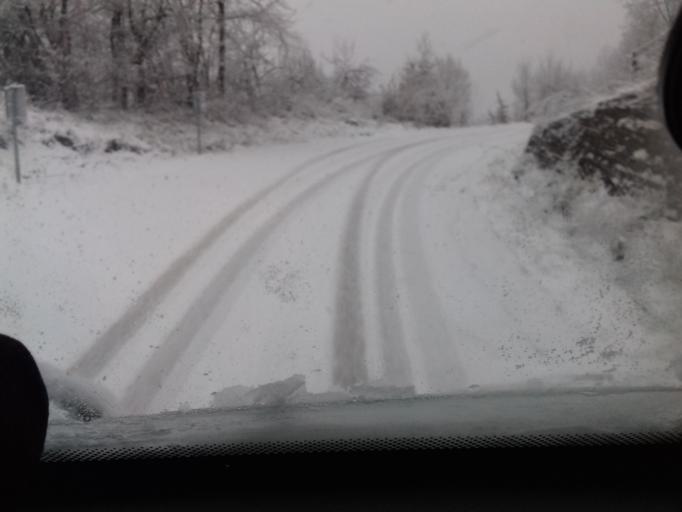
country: BA
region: Federation of Bosnia and Herzegovina
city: Lokvine
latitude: 44.2402
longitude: 17.8135
